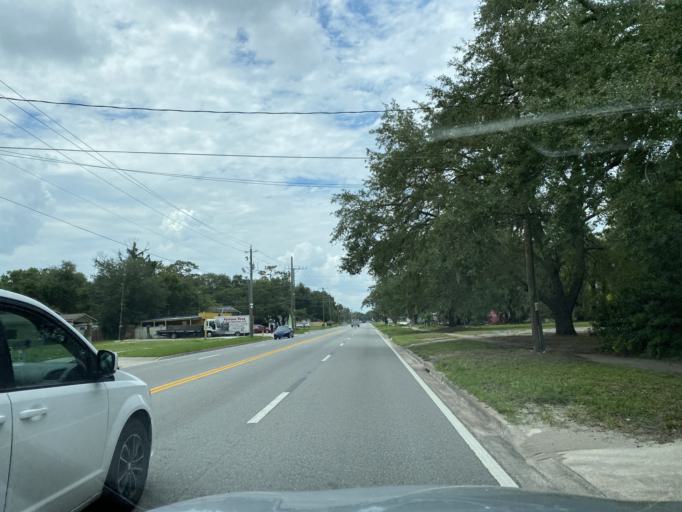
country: US
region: Florida
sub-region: Seminole County
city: Sanford
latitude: 28.7811
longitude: -81.2647
